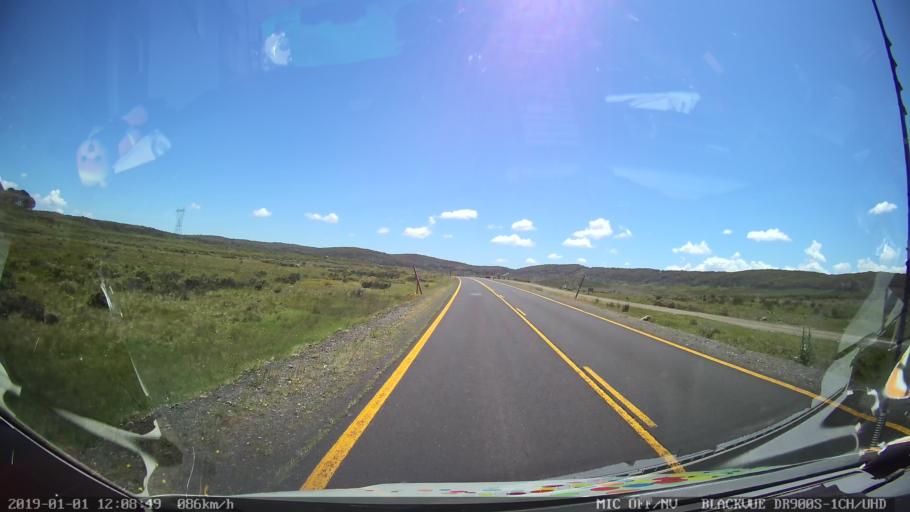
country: AU
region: New South Wales
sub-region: Tumut Shire
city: Tumut
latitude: -35.8155
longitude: 148.4963
